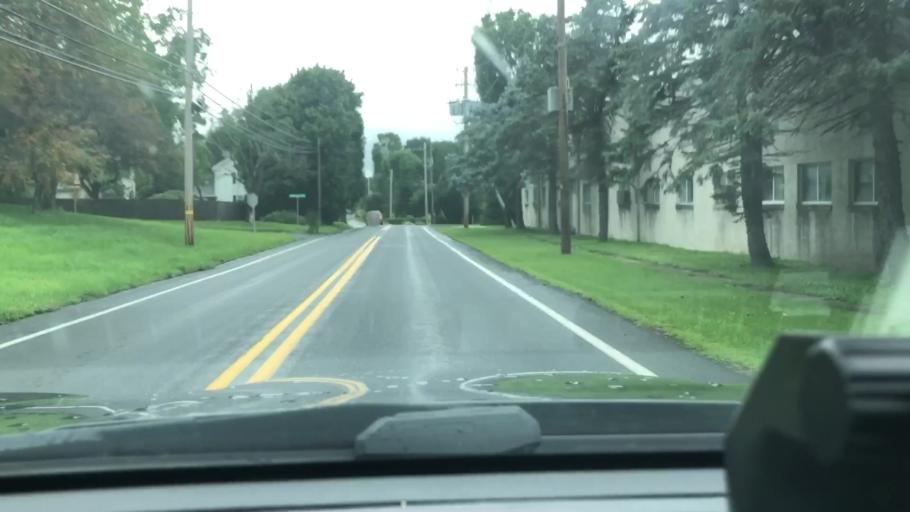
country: US
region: Pennsylvania
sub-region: Lehigh County
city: Coopersburg
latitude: 40.5019
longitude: -75.3934
